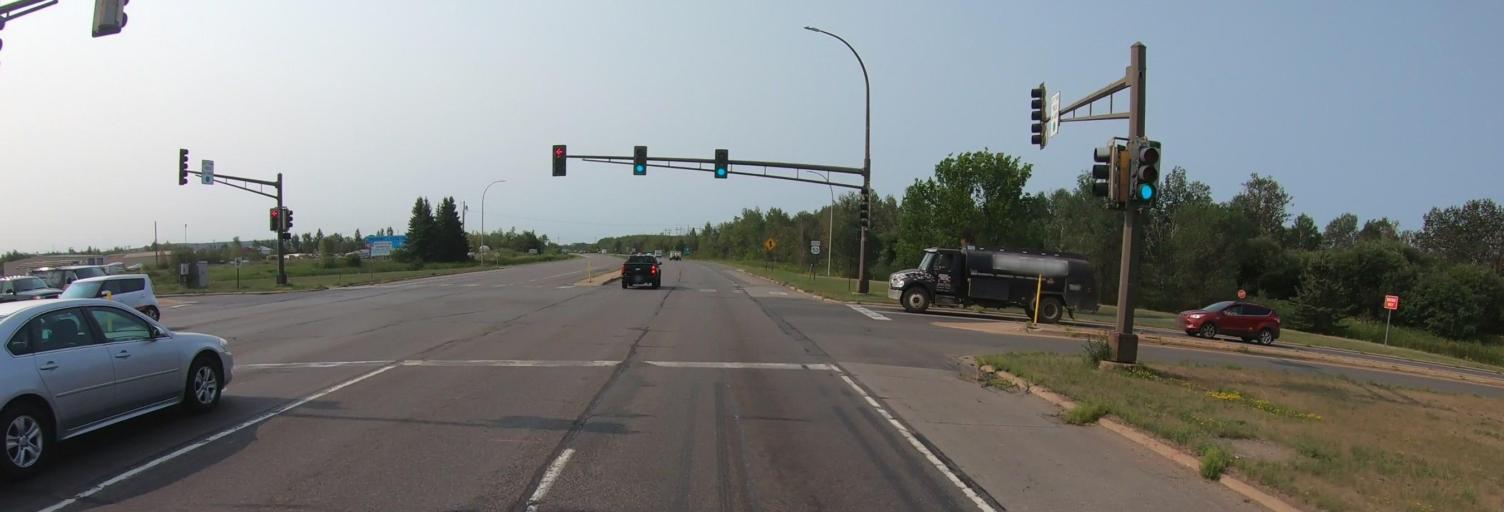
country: US
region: Minnesota
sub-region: Saint Louis County
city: Parkville
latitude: 47.5308
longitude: -92.5628
